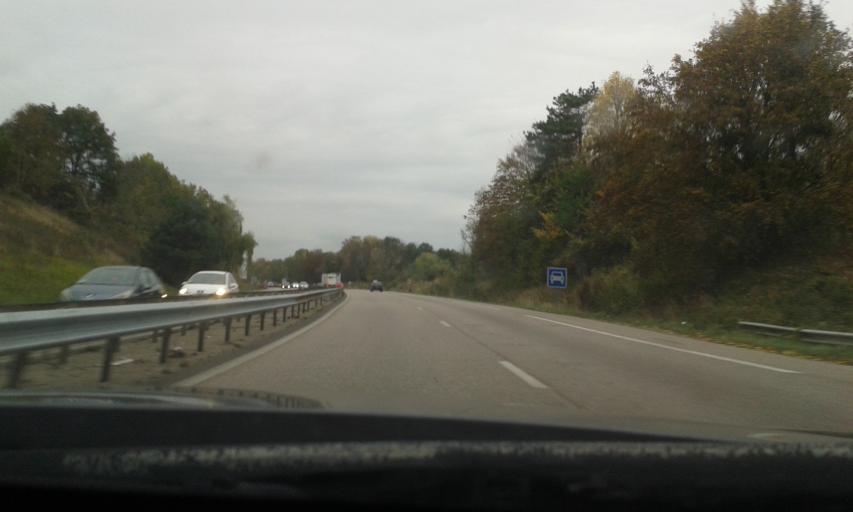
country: FR
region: Haute-Normandie
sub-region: Departement de la Seine-Maritime
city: Oissel
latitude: 49.3418
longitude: 1.0747
